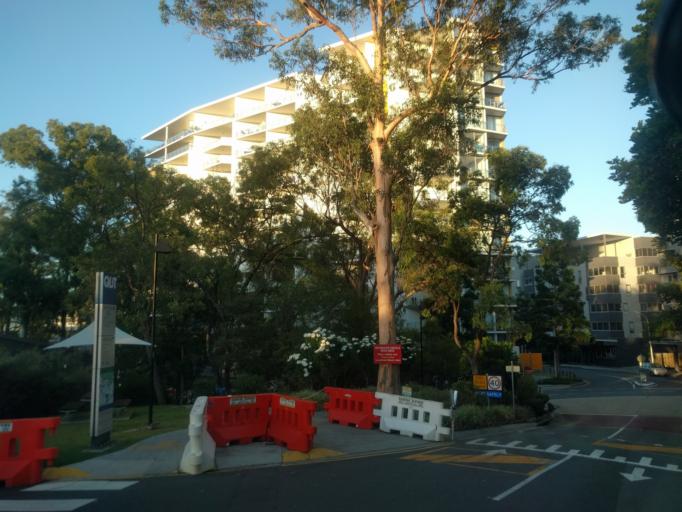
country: AU
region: Queensland
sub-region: Brisbane
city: Spring Hill
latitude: -27.4529
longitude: 153.0166
